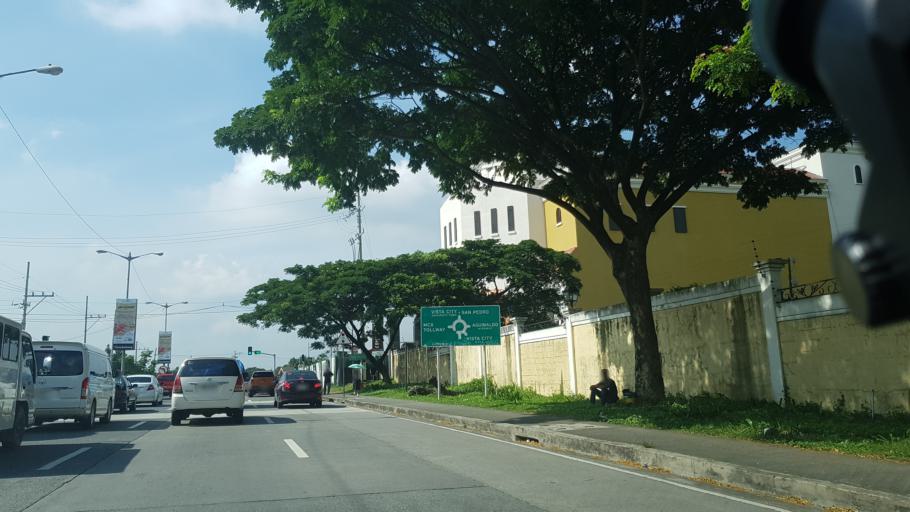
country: PH
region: Calabarzon
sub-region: Province of Laguna
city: San Pedro
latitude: 14.3774
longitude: 121.0129
